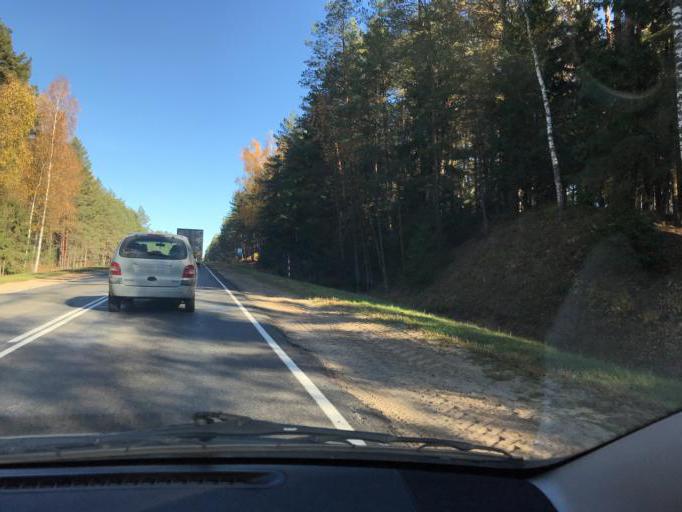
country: BY
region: Vitebsk
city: Polatsk
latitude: 55.3424
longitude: 28.7947
